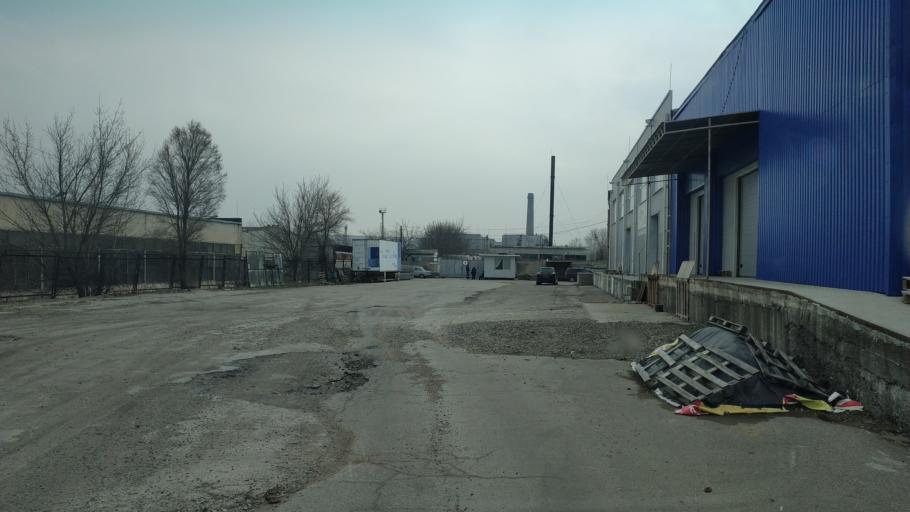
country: MD
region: Chisinau
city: Singera
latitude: 46.9114
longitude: 29.0118
